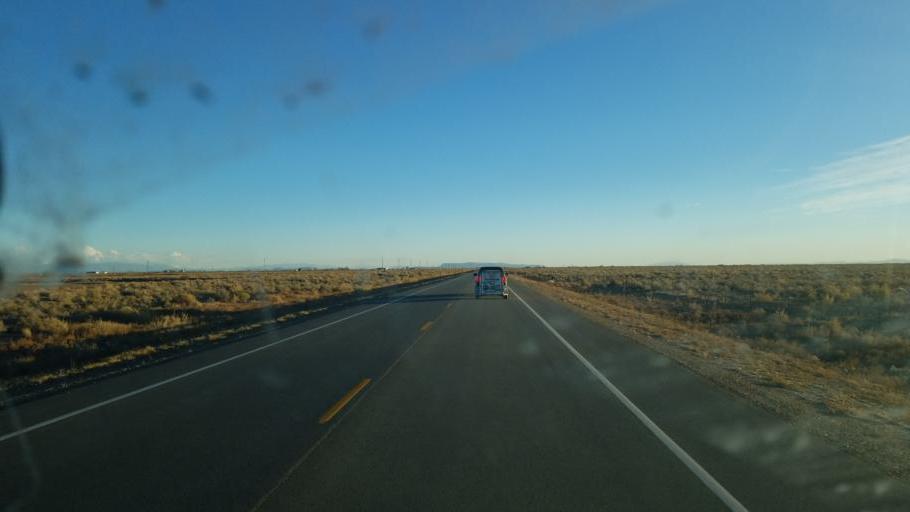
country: US
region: Colorado
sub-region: Alamosa County
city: Alamosa East
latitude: 37.6210
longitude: -105.8667
